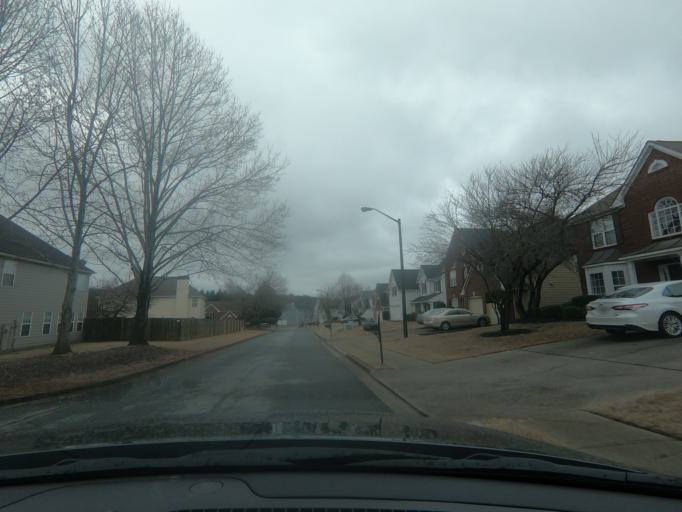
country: US
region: Georgia
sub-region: Cobb County
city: Kennesaw
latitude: 34.0469
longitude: -84.6409
